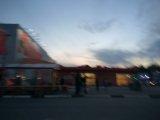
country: RU
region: Moscow
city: Strogino
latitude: 55.8114
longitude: 37.3846
